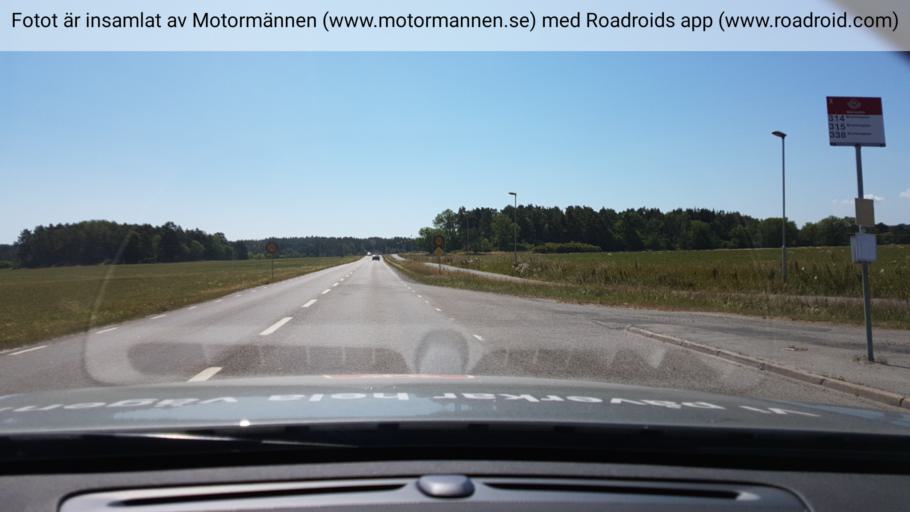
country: SE
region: Stockholm
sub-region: Ekero Kommun
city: Ekeroe
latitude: 59.3318
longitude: 17.7461
